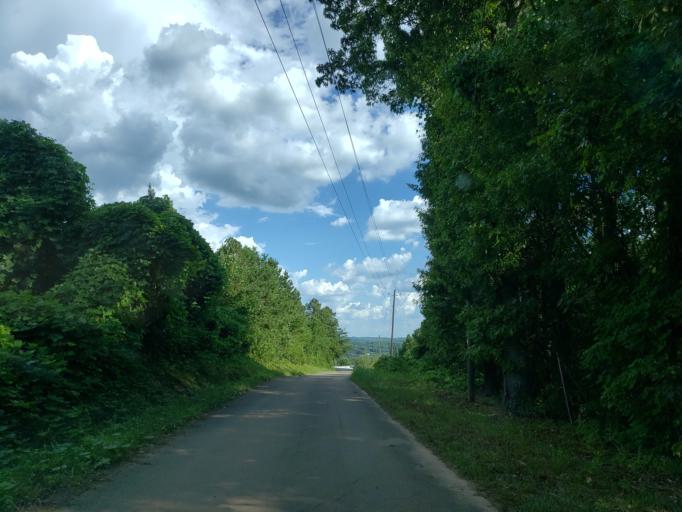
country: US
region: Georgia
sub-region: Cherokee County
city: Ball Ground
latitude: 34.3098
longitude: -84.4208
